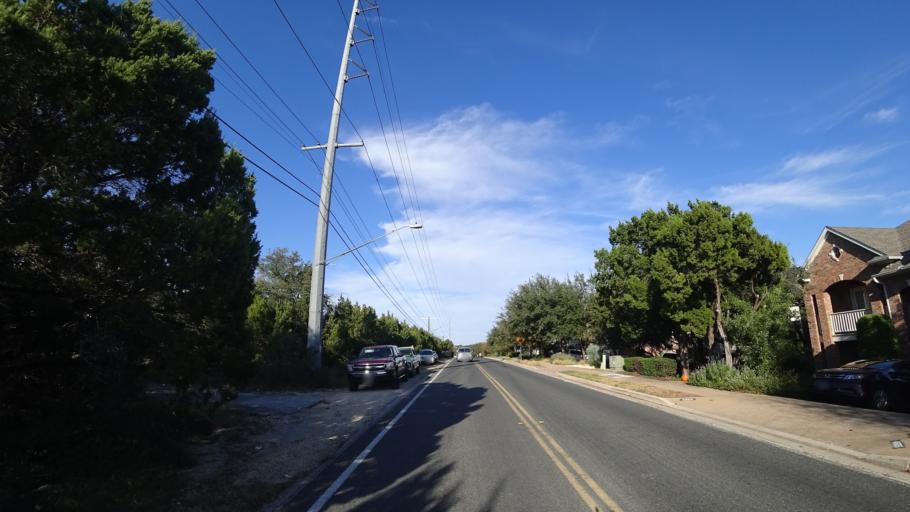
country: US
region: Texas
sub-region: Travis County
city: Barton Creek
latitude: 30.2522
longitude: -97.8470
